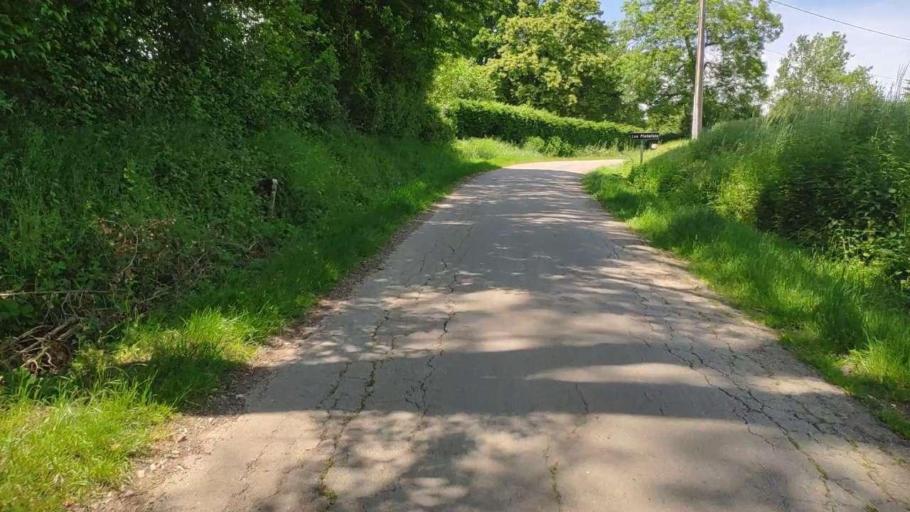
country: FR
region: Franche-Comte
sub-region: Departement du Jura
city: Bletterans
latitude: 46.7811
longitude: 5.3820
